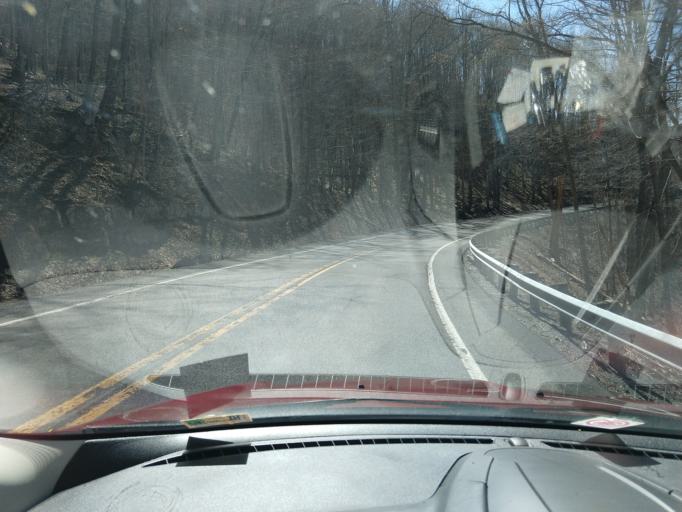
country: US
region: West Virginia
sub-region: Summers County
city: Hinton
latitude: 37.7496
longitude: -80.9108
